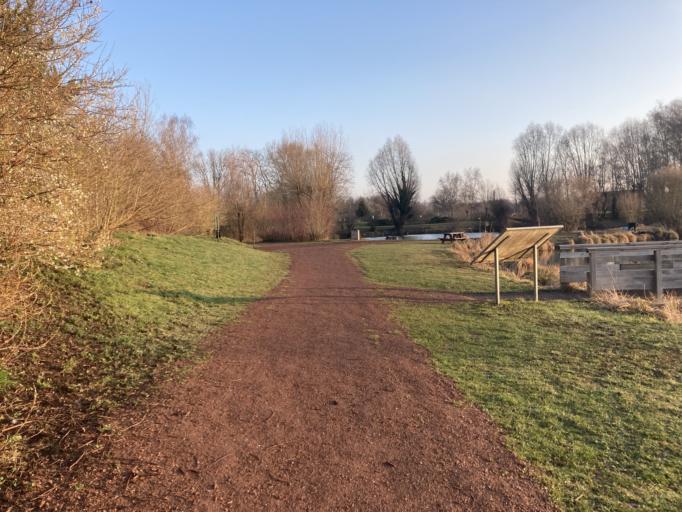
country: FR
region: Nord-Pas-de-Calais
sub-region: Departement du Pas-de-Calais
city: Labourse
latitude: 50.4984
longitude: 2.6741
